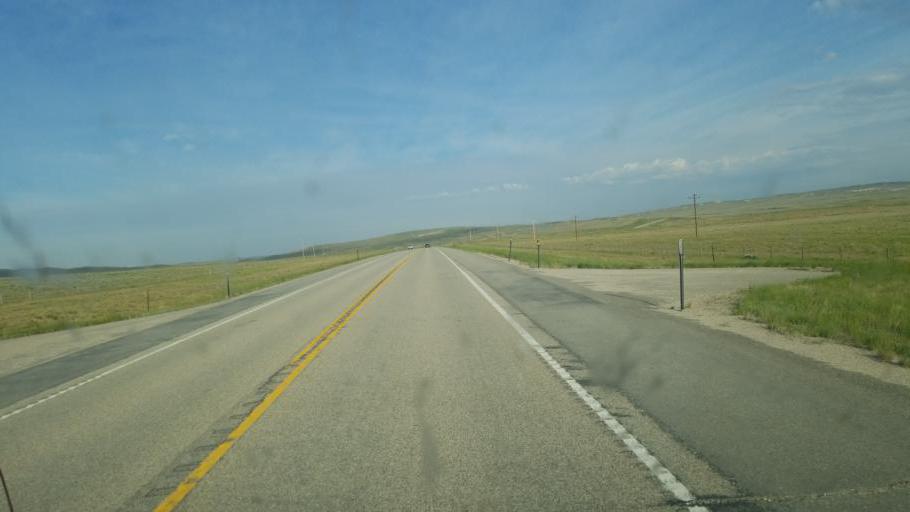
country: US
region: Wyoming
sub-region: Natrona County
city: Mills
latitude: 43.0332
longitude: -107.0074
